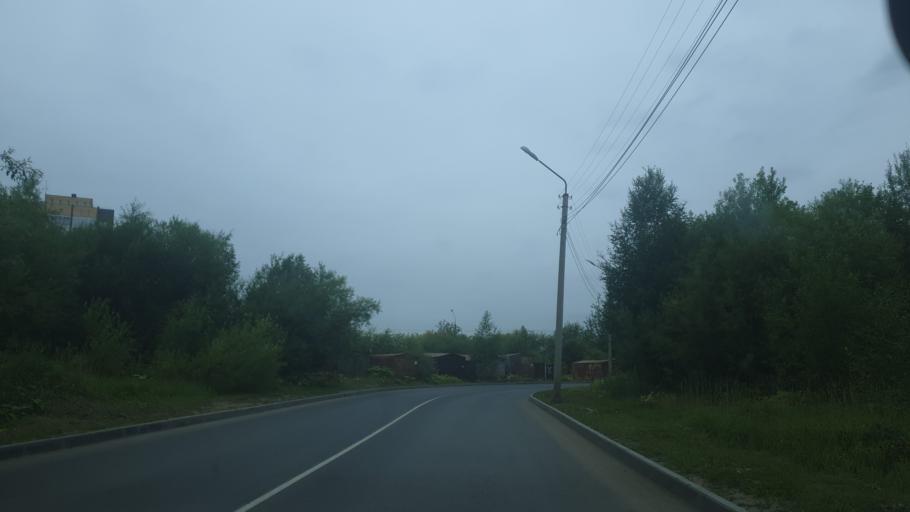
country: RU
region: Komi Republic
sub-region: Syktyvdinskiy Rayon
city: Syktyvkar
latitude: 61.6949
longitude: 50.8080
